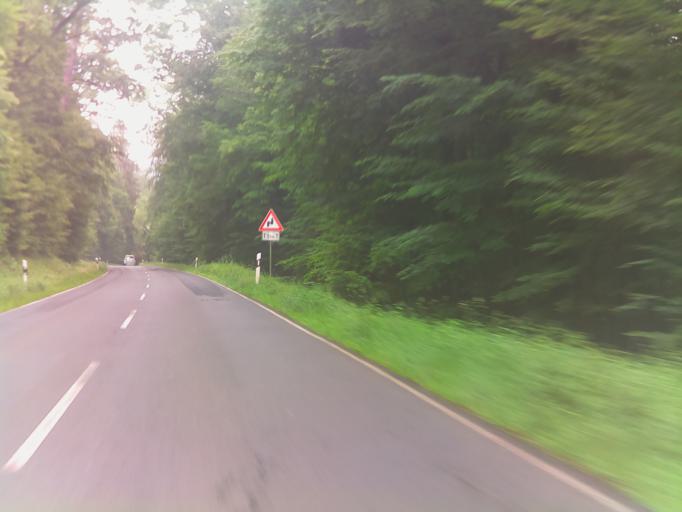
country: DE
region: Hesse
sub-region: Regierungsbezirk Darmstadt
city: Bad Soden-Salmunster
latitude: 50.2647
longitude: 9.4042
